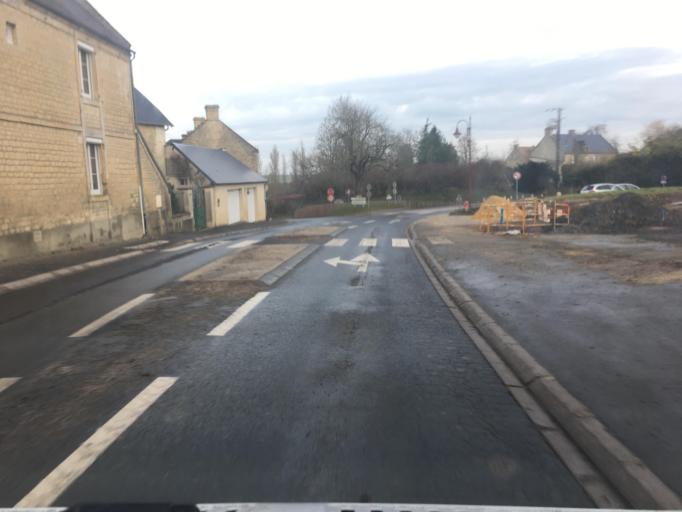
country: FR
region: Lower Normandy
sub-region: Departement du Calvados
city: Creully
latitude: 49.2518
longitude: -0.5623
